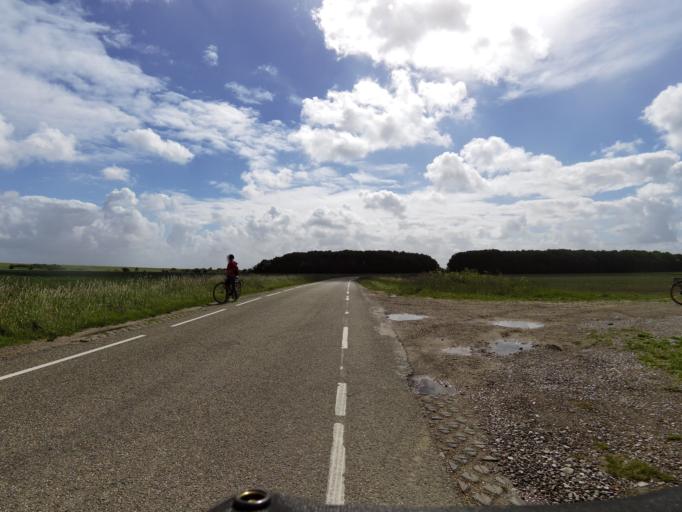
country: NL
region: Zeeland
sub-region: Schouwen-Duiveland
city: Bruinisse
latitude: 51.6837
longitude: 4.0076
